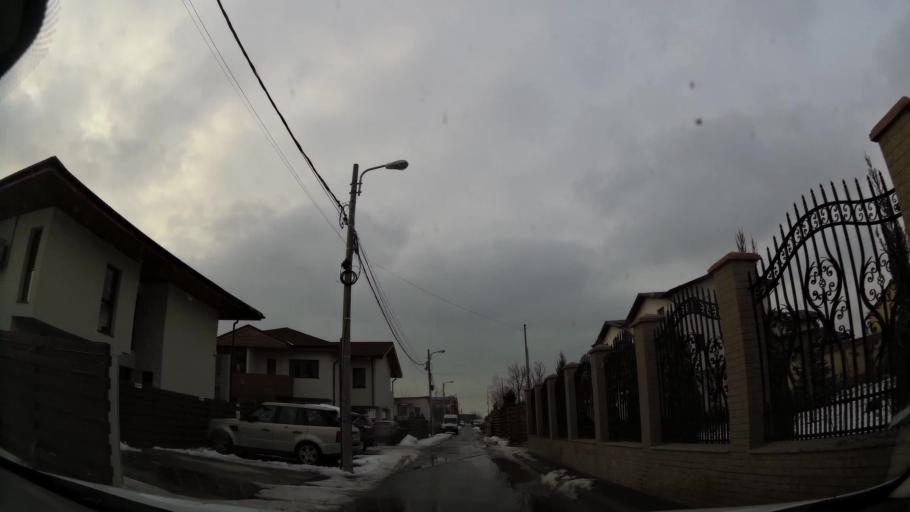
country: RO
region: Ilfov
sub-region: Voluntari City
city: Voluntari
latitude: 44.4974
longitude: 26.1647
